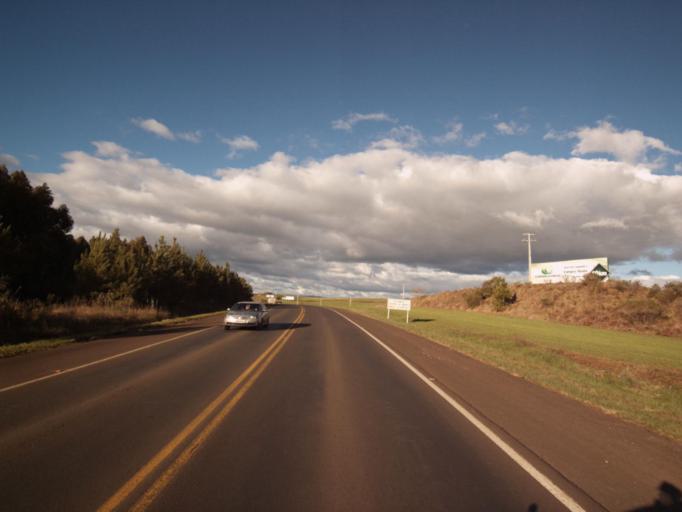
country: BR
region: Santa Catarina
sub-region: Campos Novos
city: Campos Novos
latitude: -27.3632
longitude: -51.3096
